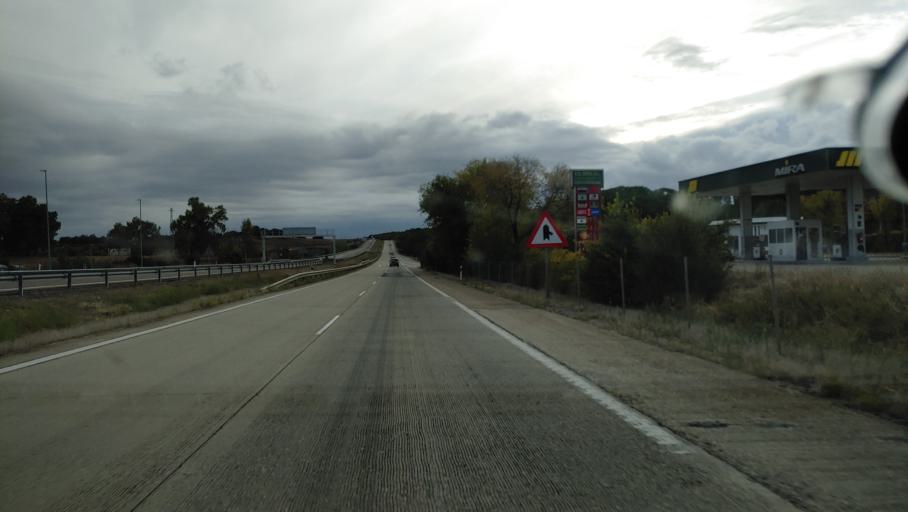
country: ES
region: Andalusia
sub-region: Provincia de Jaen
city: Santa Elena
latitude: 38.3299
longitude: -3.5447
